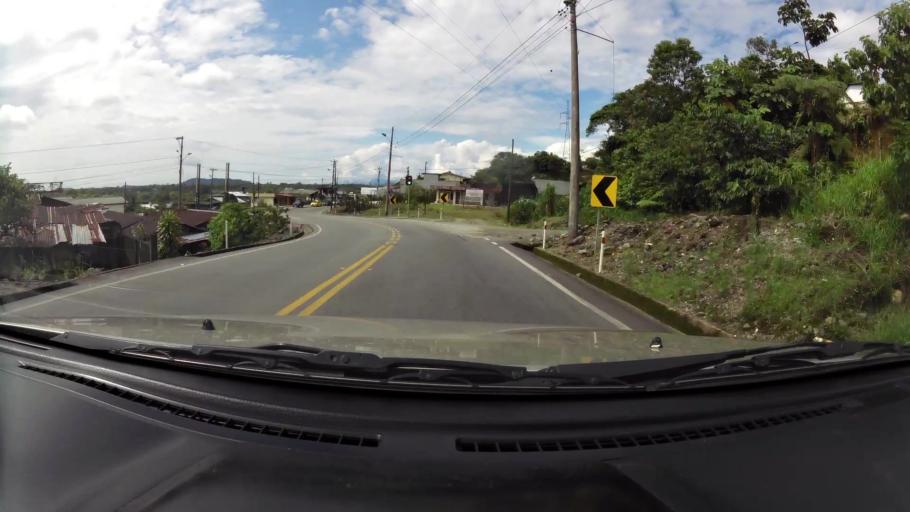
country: EC
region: Pastaza
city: Puyo
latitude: -1.4929
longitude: -78.0181
